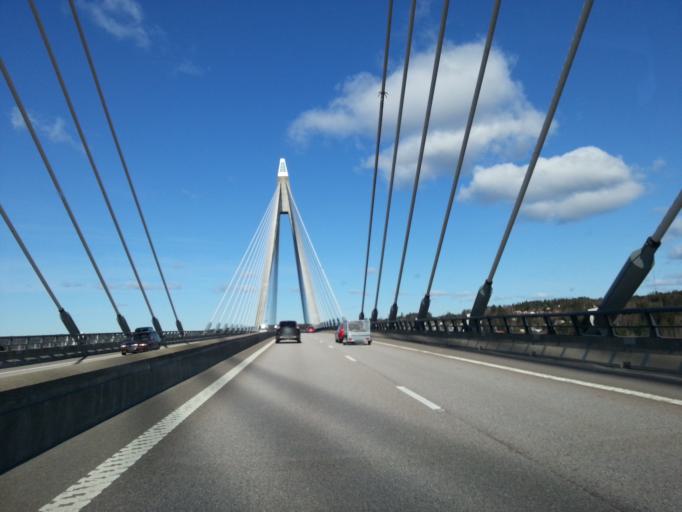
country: SE
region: Vaestra Goetaland
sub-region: Uddevalla Kommun
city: Uddevalla
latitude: 58.3250
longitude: 11.8458
